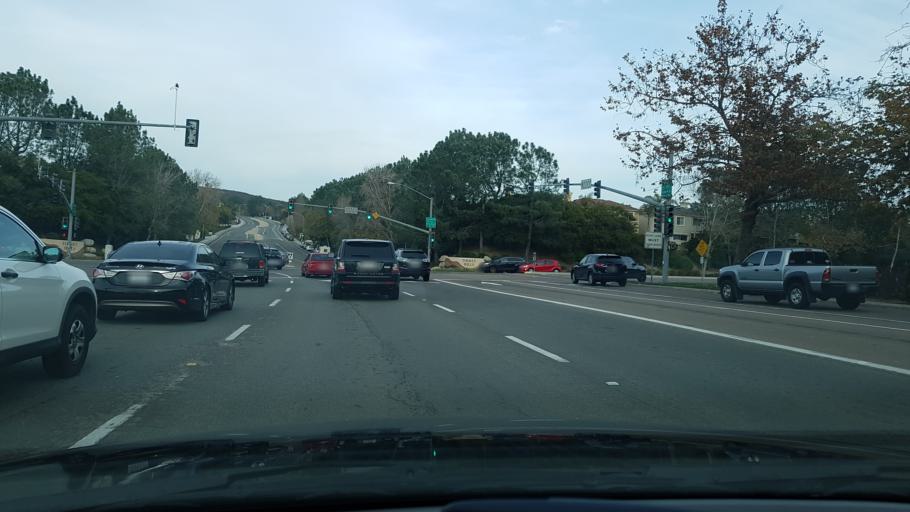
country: US
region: California
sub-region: San Diego County
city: Del Mar
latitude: 32.9218
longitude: -117.2290
